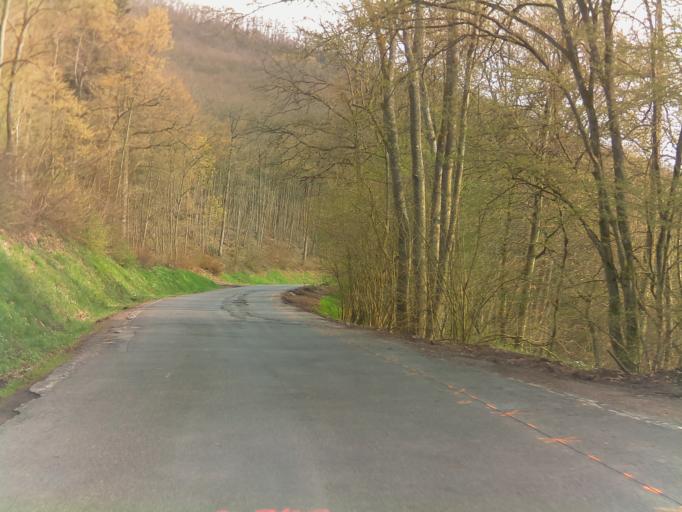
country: DE
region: Rheinland-Pfalz
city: Allenfeld
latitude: 49.8450
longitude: 7.6642
